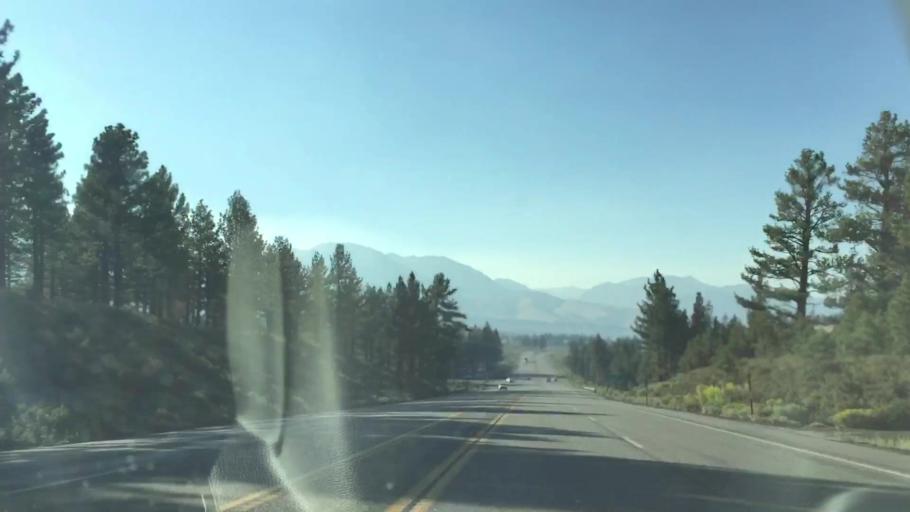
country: US
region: California
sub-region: Mono County
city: Mammoth Lakes
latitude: 37.8099
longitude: -119.0499
